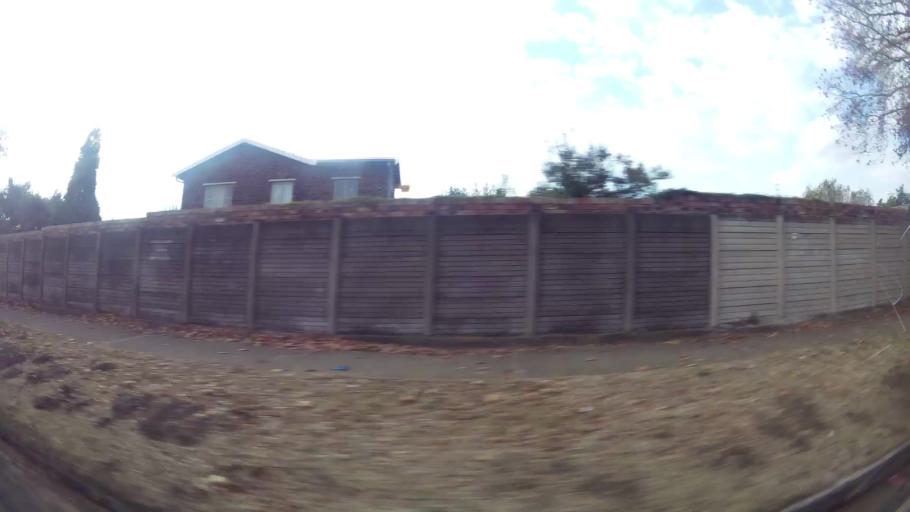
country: ZA
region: Orange Free State
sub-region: Fezile Dabi District Municipality
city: Sasolburg
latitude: -26.8100
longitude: 27.8229
